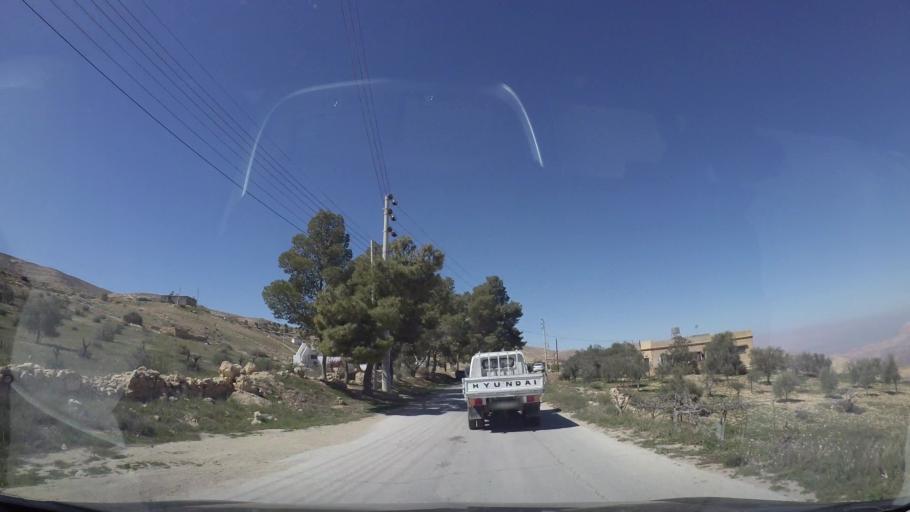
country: JO
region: Tafielah
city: At Tafilah
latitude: 30.8390
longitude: 35.5731
